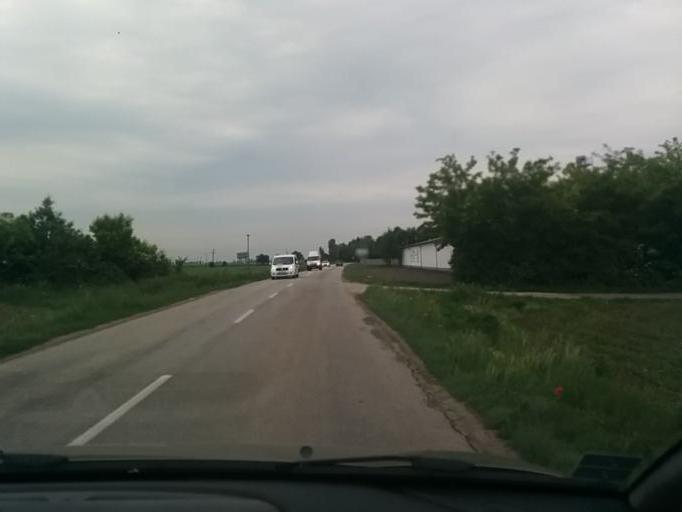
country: SK
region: Trnavsky
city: Sladkovicovo
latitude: 48.2177
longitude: 17.5951
